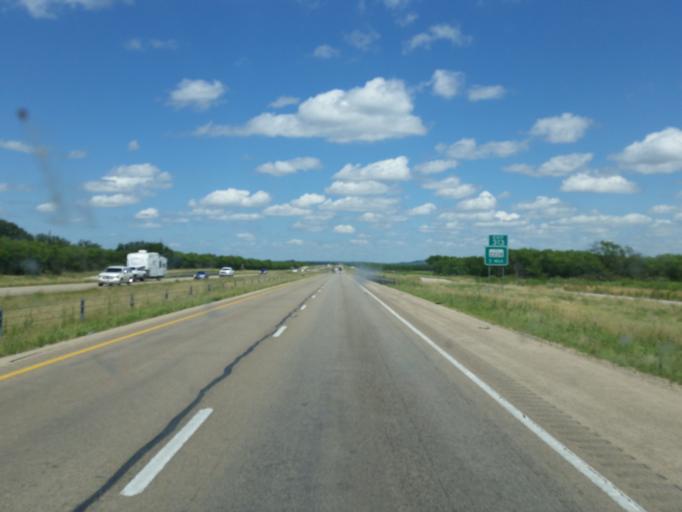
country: US
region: Texas
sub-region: Callahan County
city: Baird
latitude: 32.3883
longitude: -99.3194
